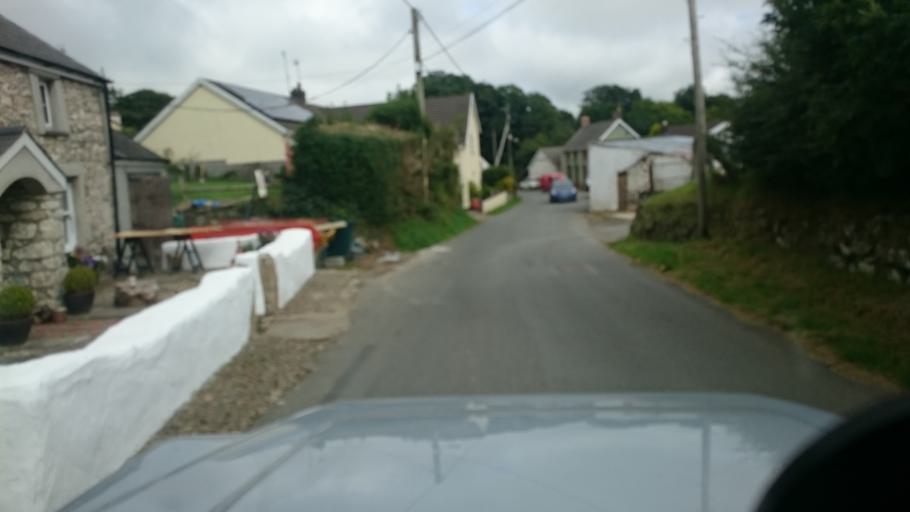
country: GB
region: Wales
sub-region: Pembrokeshire
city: Ambleston
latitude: 51.9228
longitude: -4.9418
